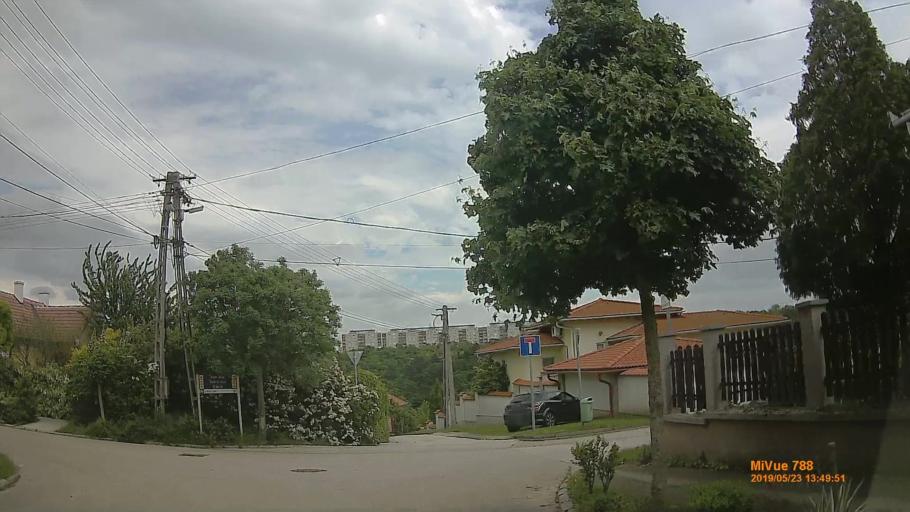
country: HU
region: Veszprem
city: Veszprem
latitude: 47.1029
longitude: 17.9056
